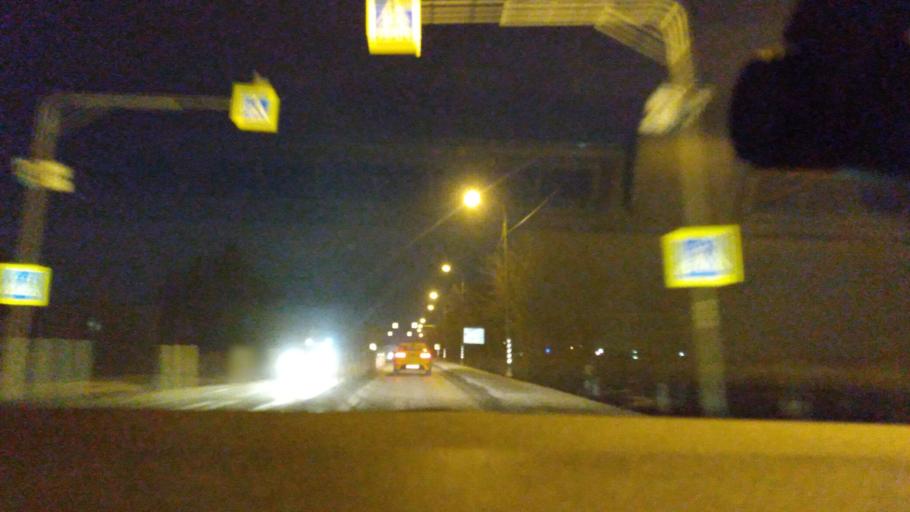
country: RU
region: Moskovskaya
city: Zagoryanskiy
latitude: 55.9510
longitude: 37.9547
